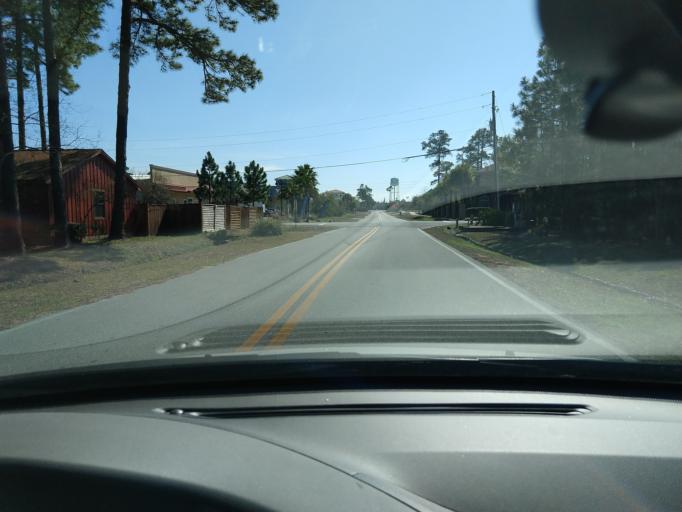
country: US
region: Florida
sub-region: Walton County
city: Miramar Beach
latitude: 30.3864
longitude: -86.3606
